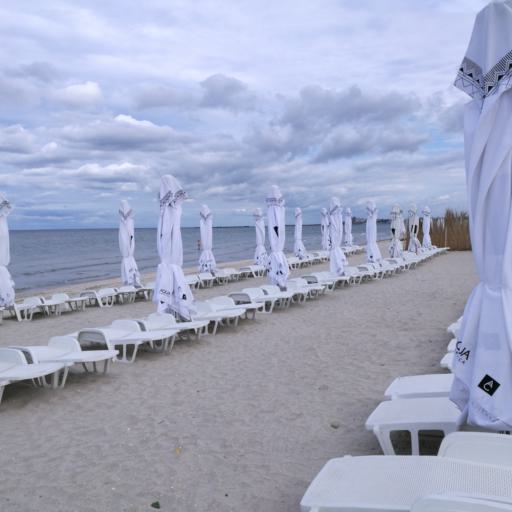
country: RO
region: Constanta
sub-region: Municipiul Constanta
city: Palazu Mare
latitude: 44.2487
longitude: 28.6229
